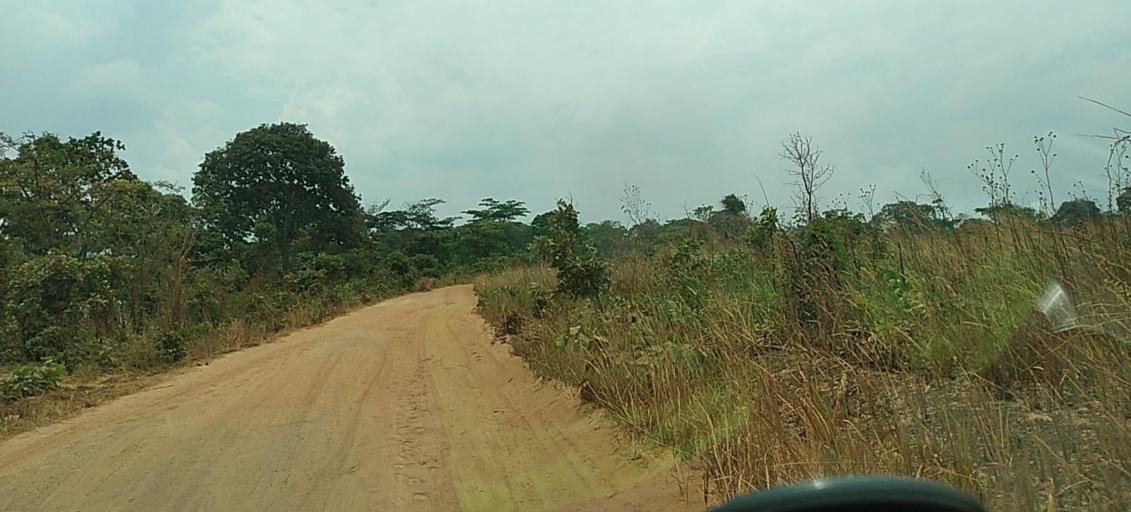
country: ZM
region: North-Western
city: Kansanshi
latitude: -12.0453
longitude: 26.3336
